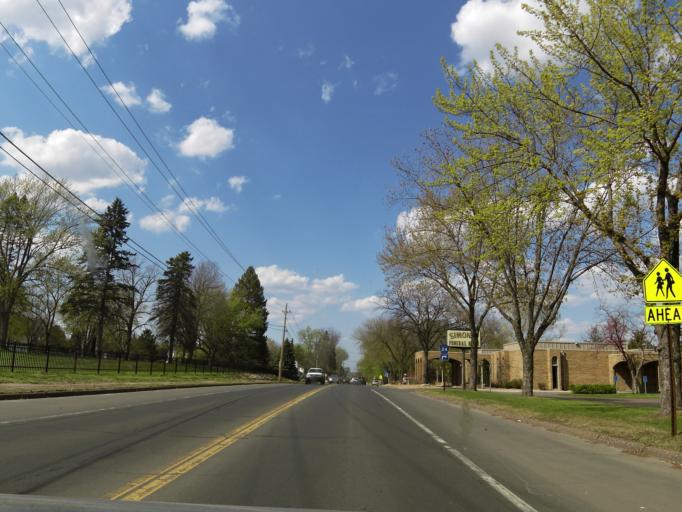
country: US
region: Minnesota
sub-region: Washington County
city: Stillwater
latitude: 45.0415
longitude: -92.8076
